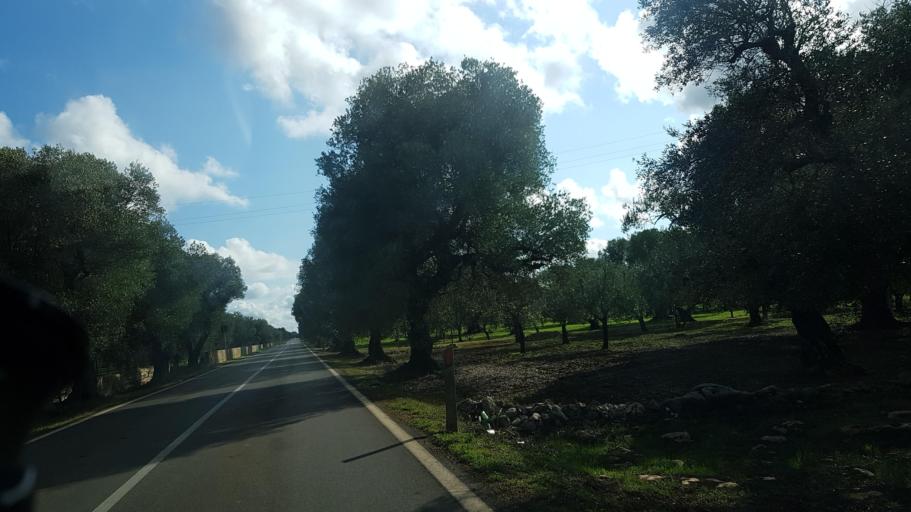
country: IT
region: Apulia
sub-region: Provincia di Brindisi
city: San Michele Salentino
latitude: 40.6536
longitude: 17.6047
